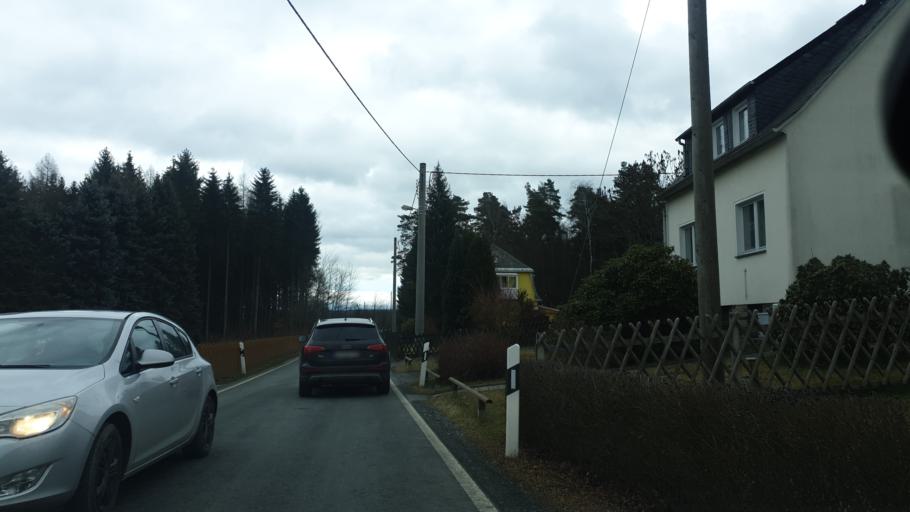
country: DE
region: Saxony
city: Bad Elster
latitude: 50.2744
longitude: 12.2710
